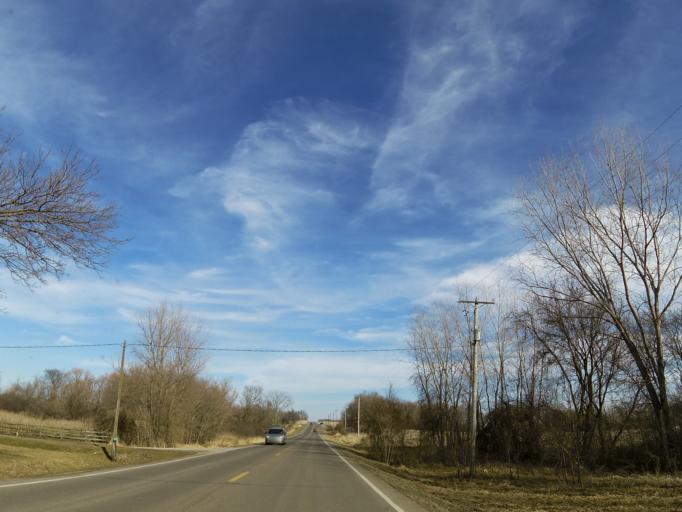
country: US
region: Minnesota
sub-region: Rice County
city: Northfield
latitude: 44.4858
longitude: -93.1877
